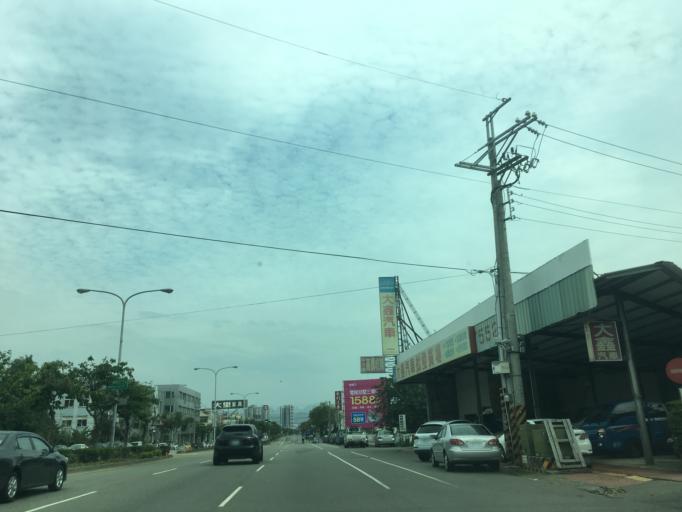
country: TW
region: Taiwan
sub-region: Taichung City
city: Taichung
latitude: 24.1084
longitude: 120.6625
